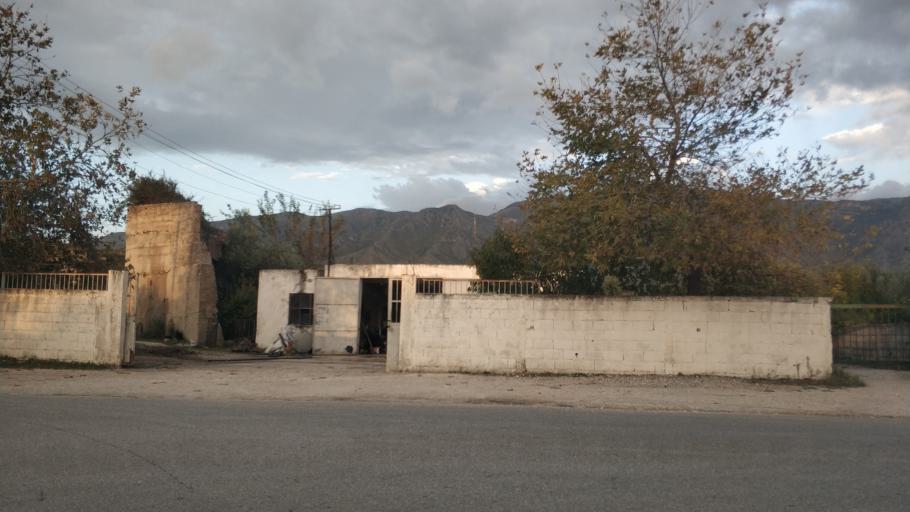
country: AL
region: Vlore
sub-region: Rrethi i Vlores
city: Orikum
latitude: 40.3300
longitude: 19.4772
